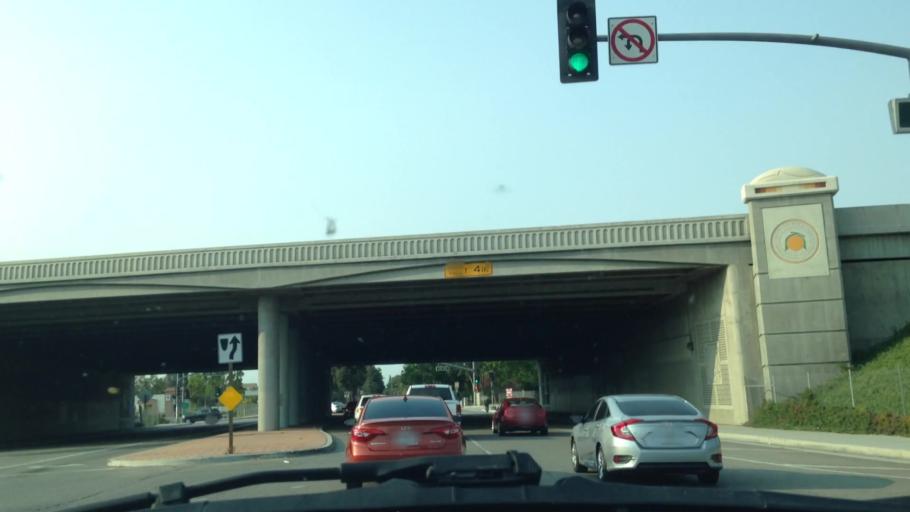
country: US
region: California
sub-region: Orange County
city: Orange
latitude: 33.7750
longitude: -117.8531
